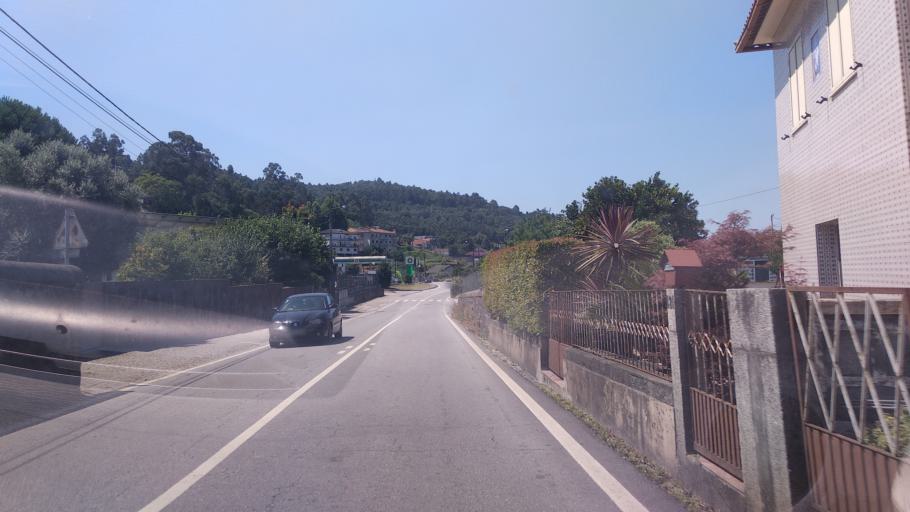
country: PT
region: Braga
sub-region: Braga
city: Adaufe
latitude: 41.5840
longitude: -8.4047
